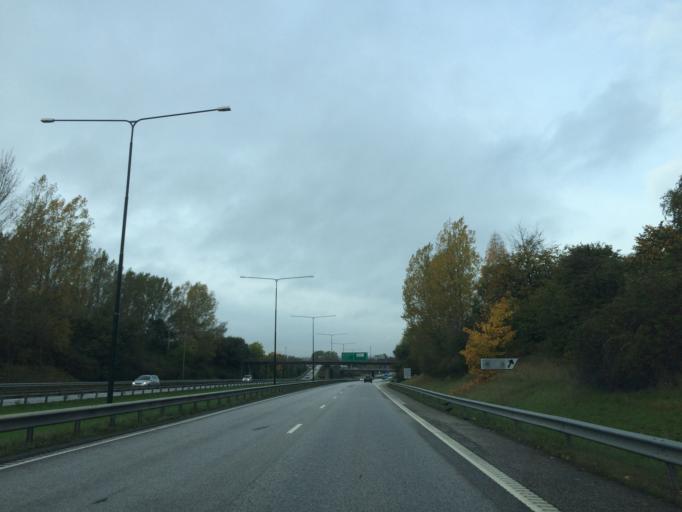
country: SE
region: Skane
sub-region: Malmo
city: Malmoe
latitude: 55.5640
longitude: 13.0166
